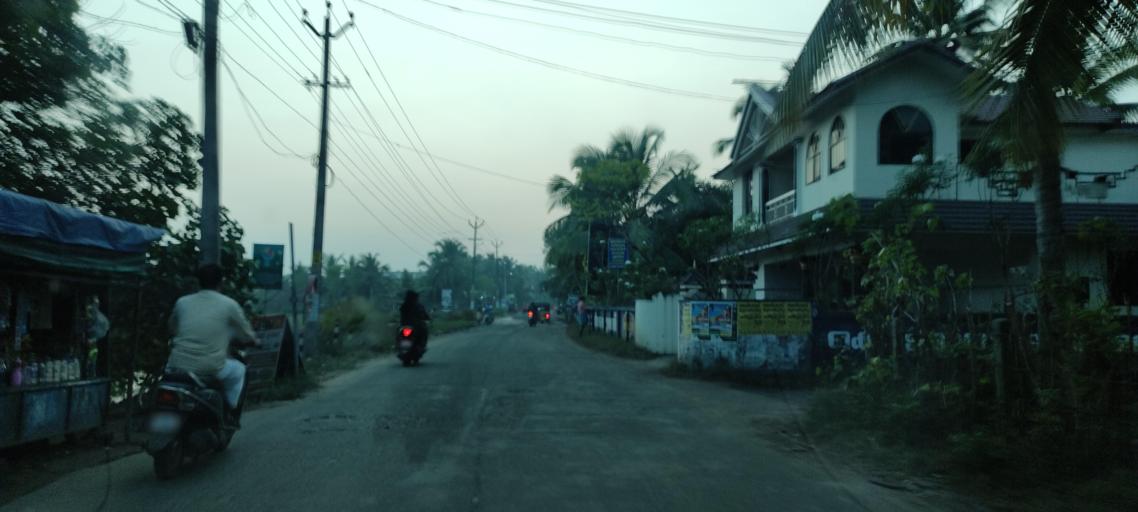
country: IN
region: Kerala
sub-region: Alappuzha
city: Kayankulam
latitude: 9.1188
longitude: 76.4866
